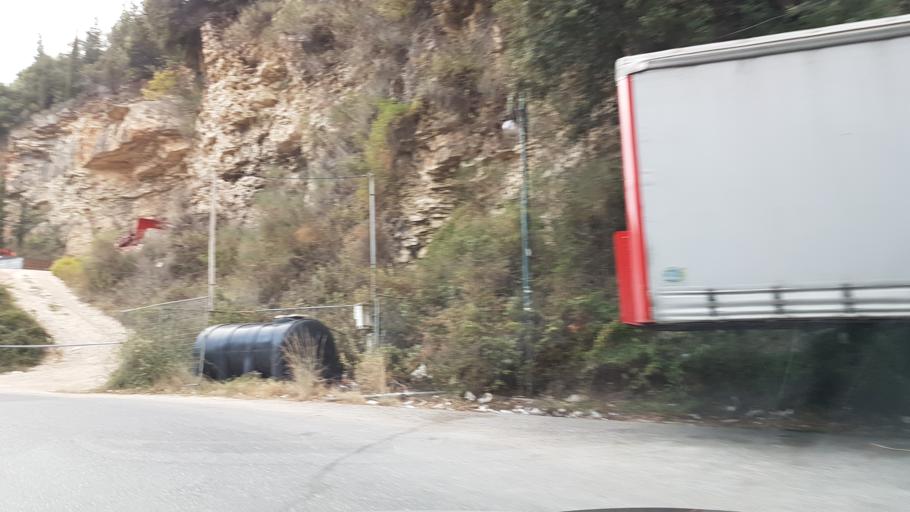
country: GR
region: Ionian Islands
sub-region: Nomos Kerkyras
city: Kontokali
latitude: 39.7359
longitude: 19.9190
